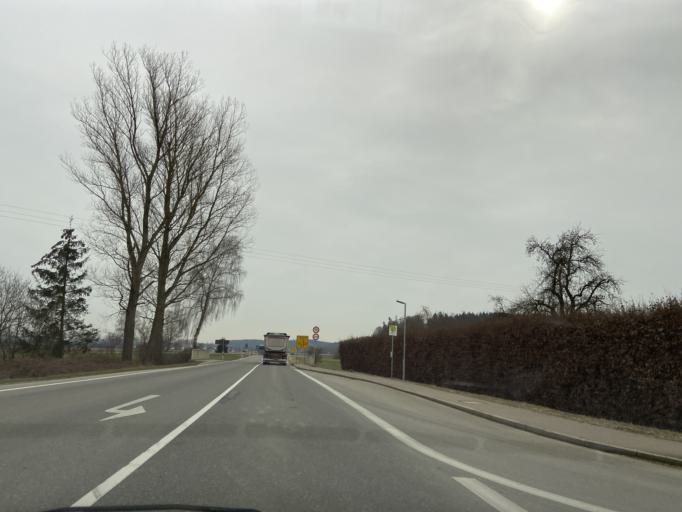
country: DE
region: Baden-Wuerttemberg
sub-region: Tuebingen Region
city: Ostrach
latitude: 47.9829
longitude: 9.3403
